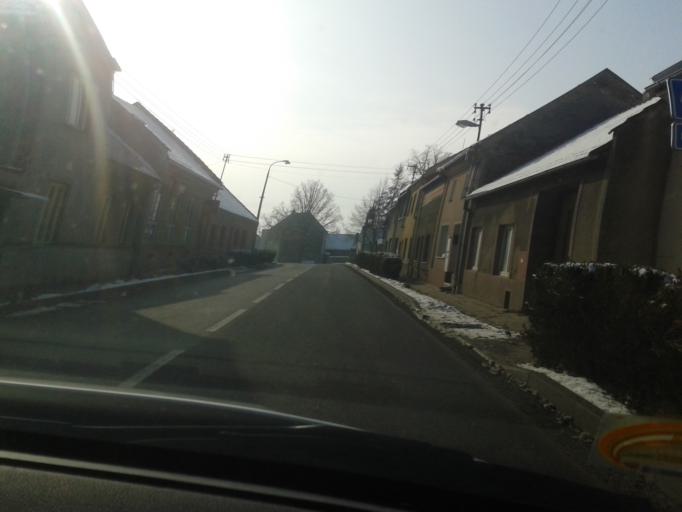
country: CZ
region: Olomoucky
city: Celechovice na Hane
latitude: 49.5315
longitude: 17.1019
